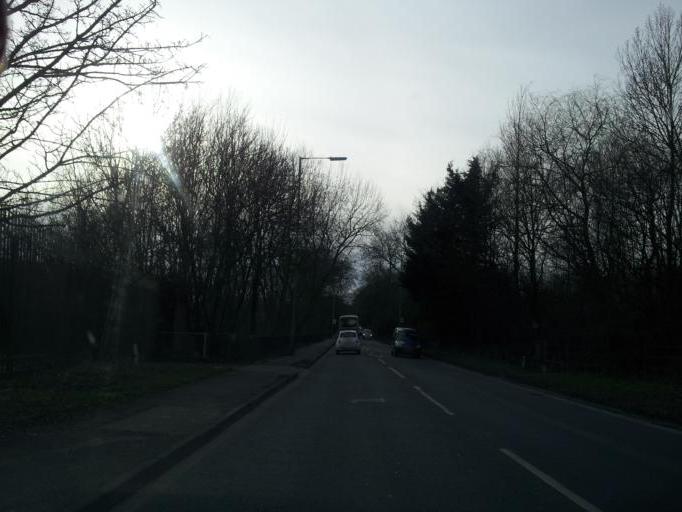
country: GB
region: England
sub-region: Hertfordshire
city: Elstree
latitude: 51.6425
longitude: -0.3229
